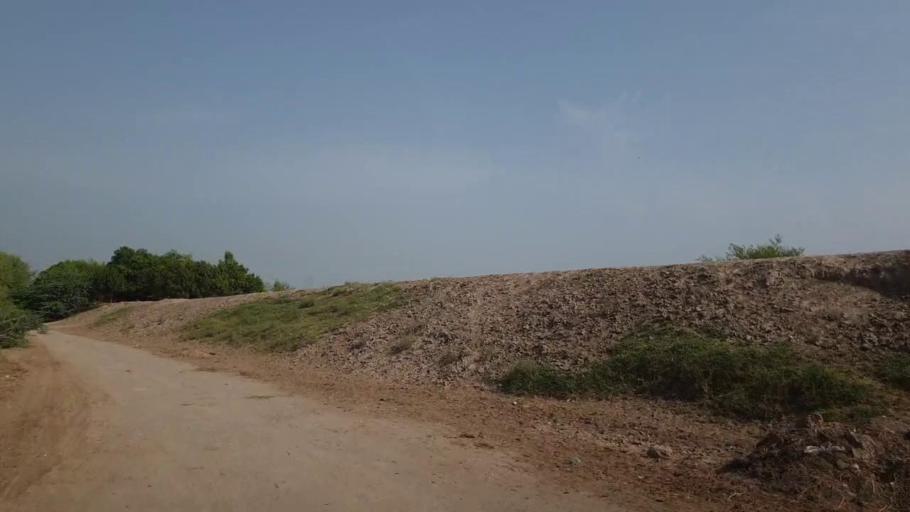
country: PK
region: Sindh
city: Larkana
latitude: 27.4795
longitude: 68.2568
